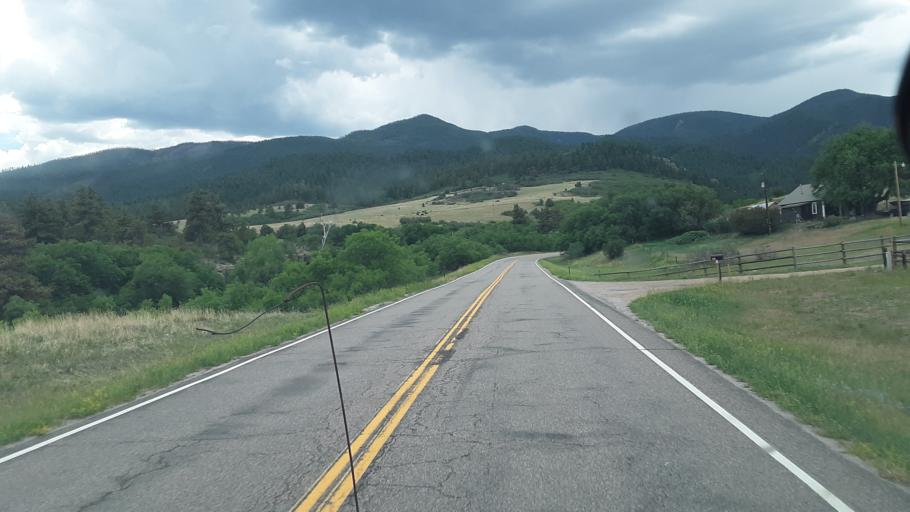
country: US
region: Colorado
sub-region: Fremont County
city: Florence
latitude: 38.1842
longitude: -105.1054
